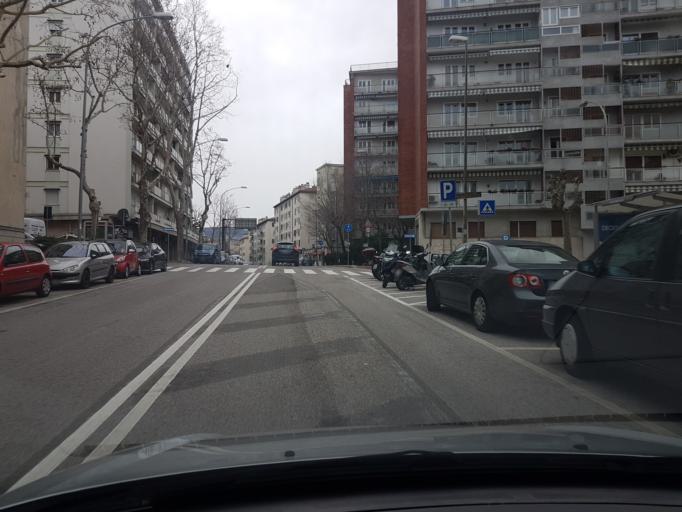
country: IT
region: Friuli Venezia Giulia
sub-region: Provincia di Trieste
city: Trieste
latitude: 45.6386
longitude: 13.7678
